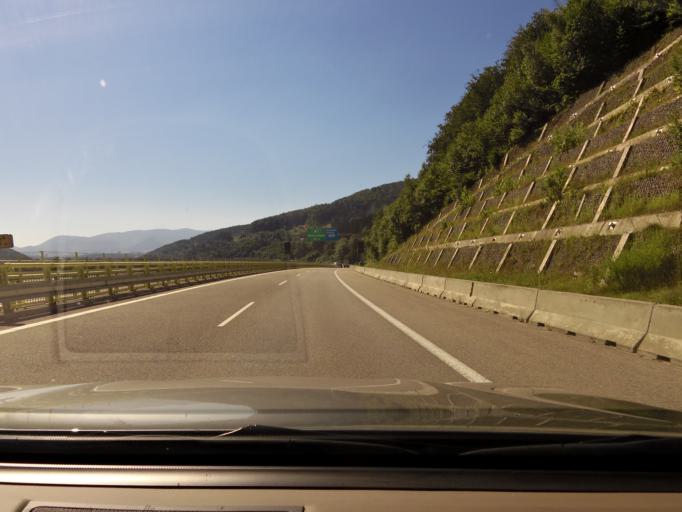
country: SK
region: Zilinsky
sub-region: Okres Zilina
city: Zilina
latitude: 49.2496
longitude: 18.6849
